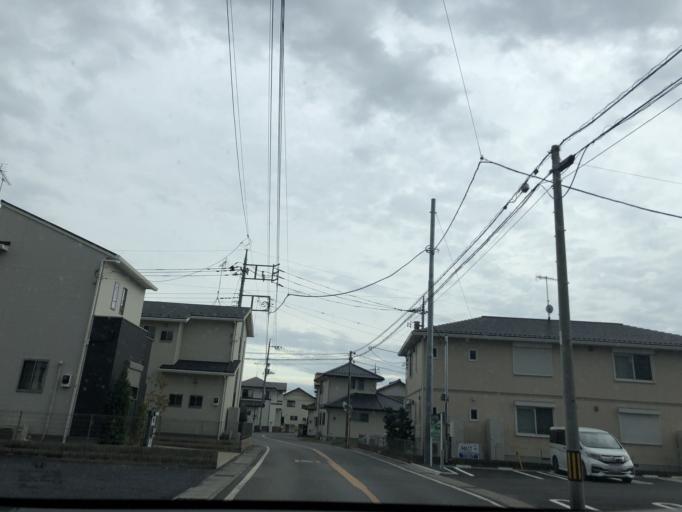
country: JP
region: Tochigi
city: Sano
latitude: 36.3095
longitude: 139.5710
